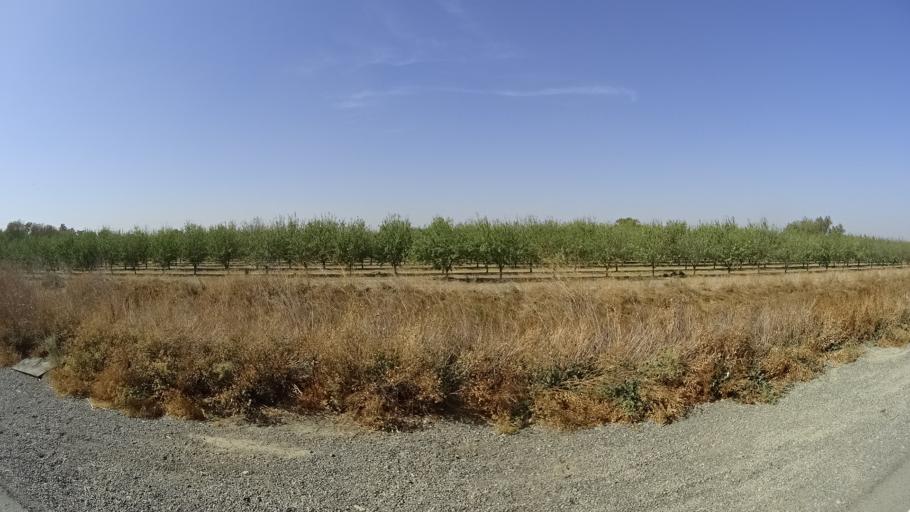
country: US
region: California
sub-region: Yolo County
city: Davis
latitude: 38.5592
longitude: -121.6756
